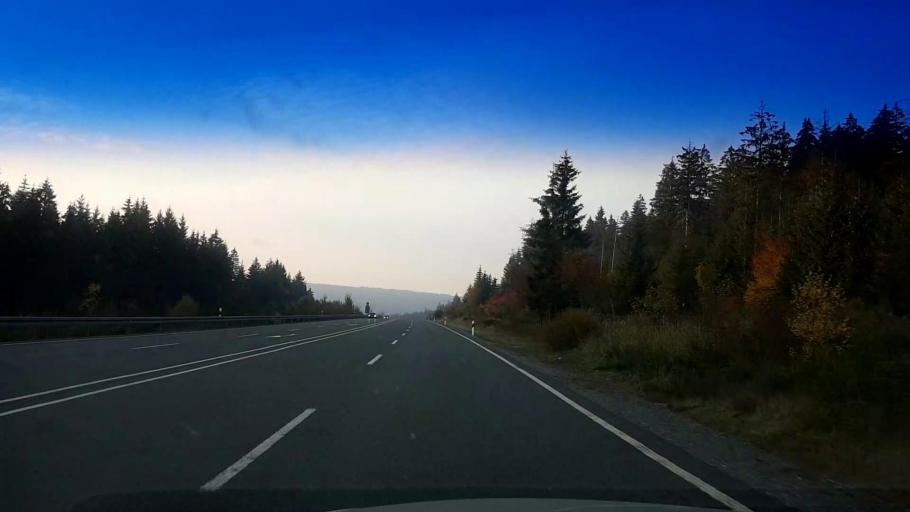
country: DE
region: Bavaria
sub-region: Upper Franconia
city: Fichtelberg
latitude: 50.0436
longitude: 11.8367
